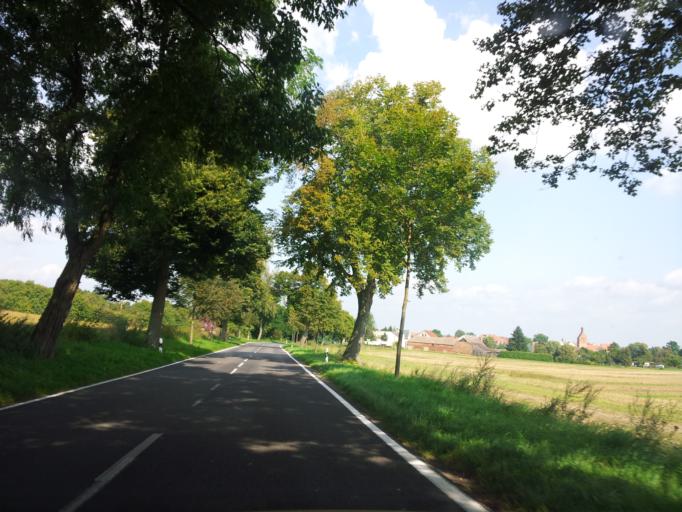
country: DE
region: Brandenburg
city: Treuenbrietzen
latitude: 52.0682
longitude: 12.9418
